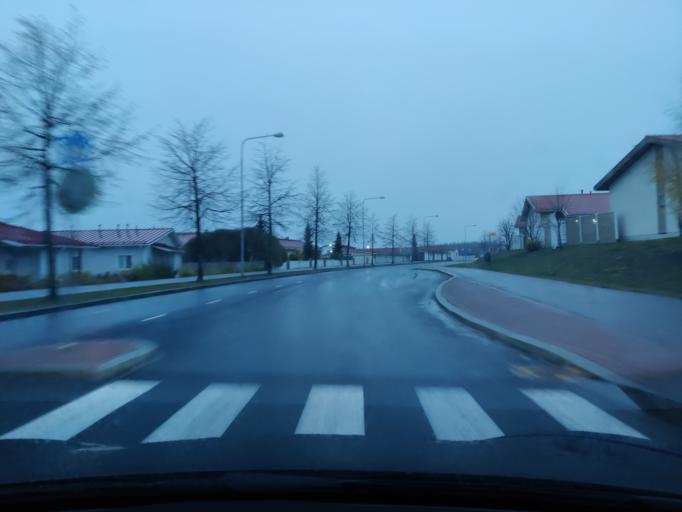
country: FI
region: Northern Savo
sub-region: Kuopio
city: Kuopio
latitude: 62.8271
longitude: 27.6816
